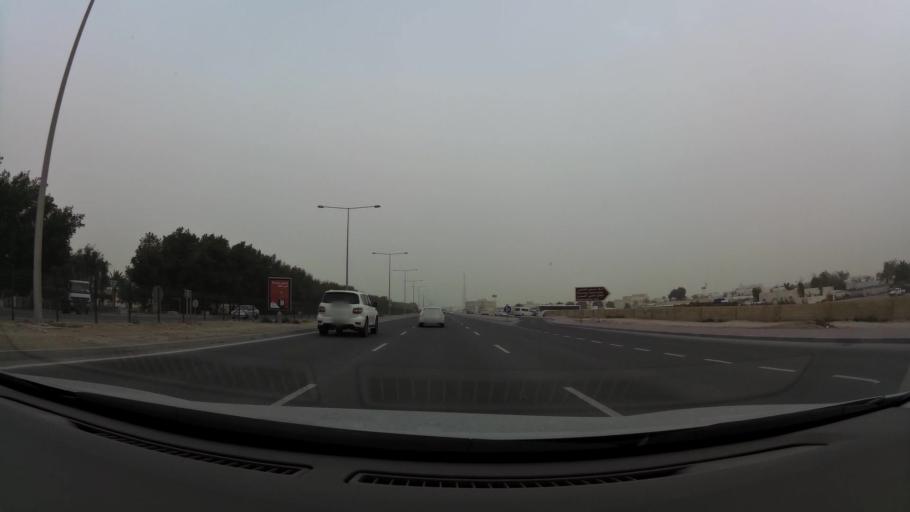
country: QA
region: Baladiyat ad Dawhah
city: Doha
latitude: 25.2369
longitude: 51.4814
